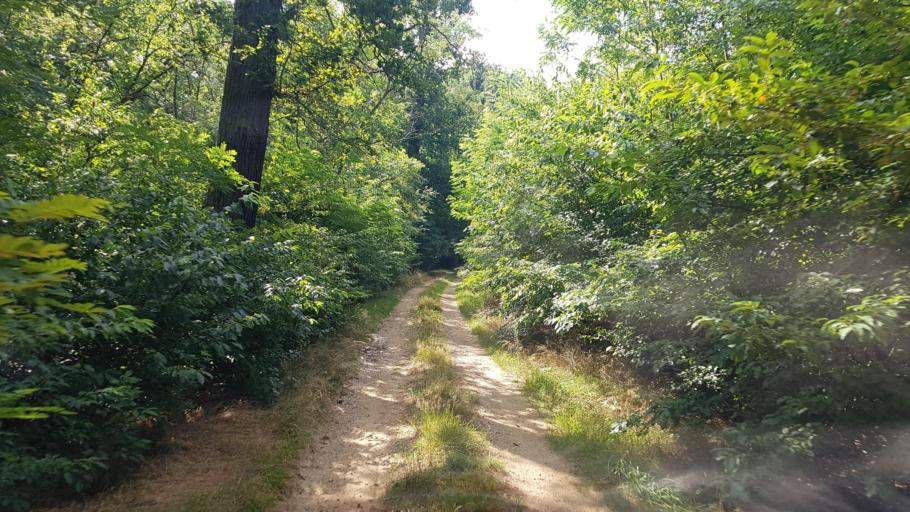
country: DE
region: Brandenburg
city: Sonnewalde
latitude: 51.7532
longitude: 13.6926
